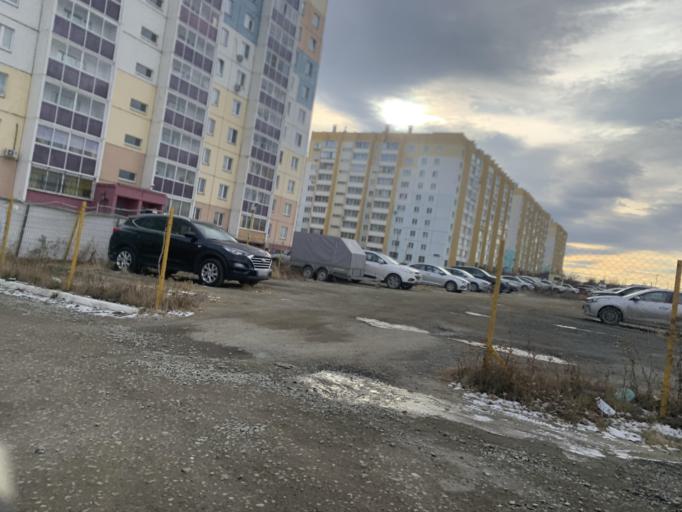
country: RU
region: Chelyabinsk
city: Roshchino
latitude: 55.1924
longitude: 61.2759
